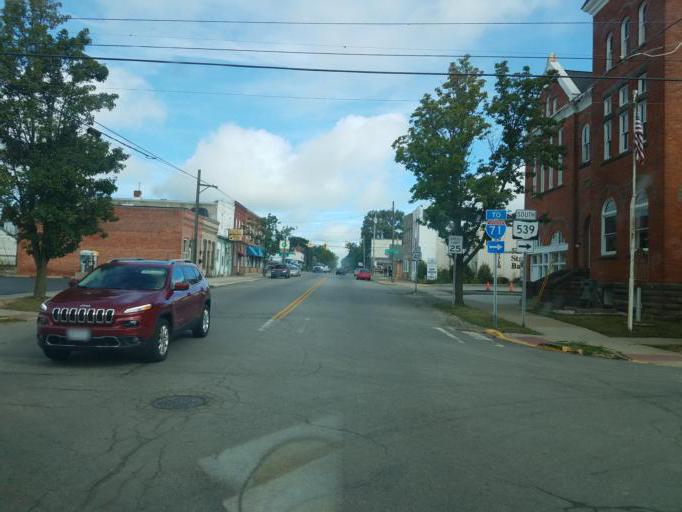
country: US
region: Ohio
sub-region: Wayne County
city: West Salem
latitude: 40.9715
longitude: -82.1097
